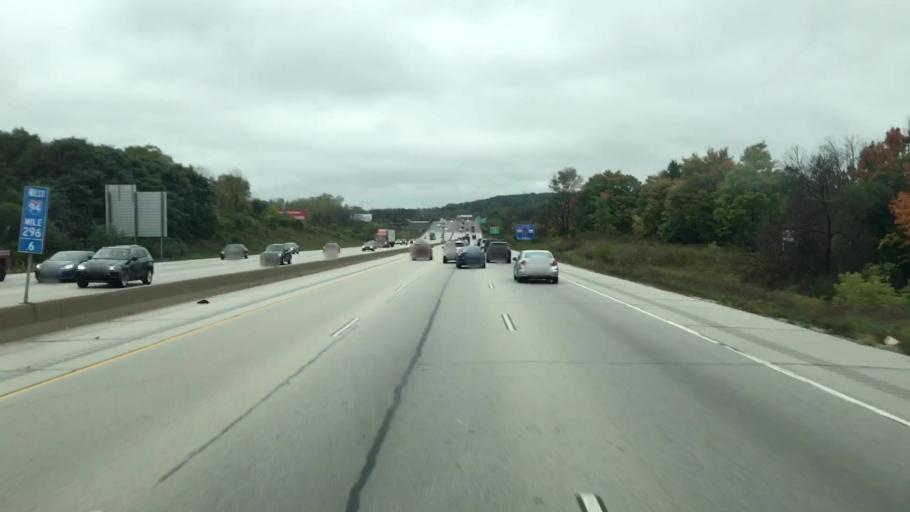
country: US
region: Wisconsin
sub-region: Waukesha County
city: Waukesha
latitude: 43.0443
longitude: -88.1940
